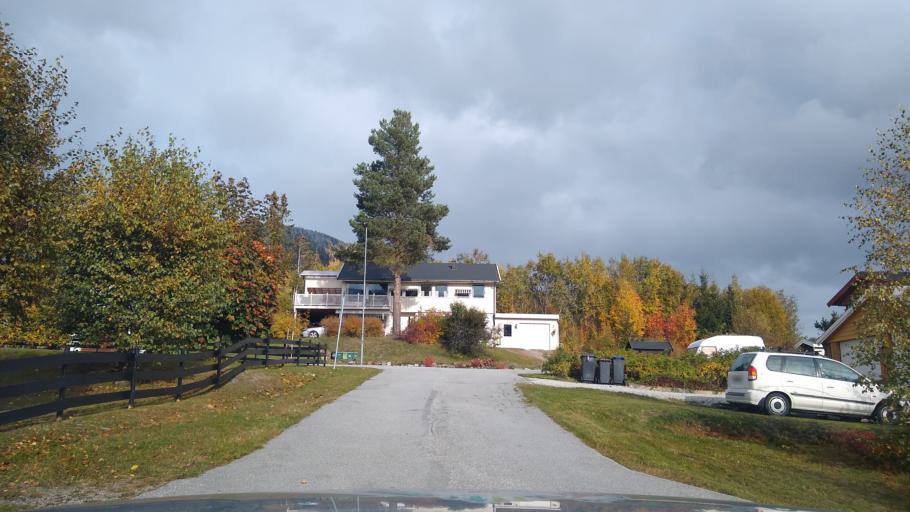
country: NO
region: Oppland
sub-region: Ringebu
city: Ringebu
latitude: 61.5412
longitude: 10.1232
